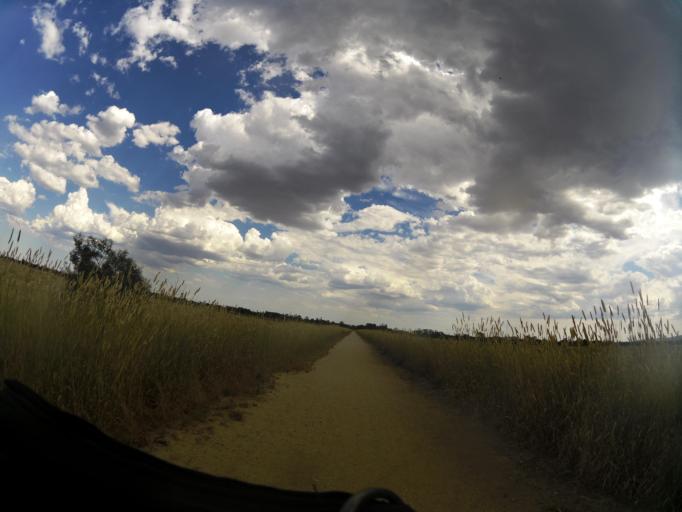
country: AU
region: Victoria
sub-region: Wellington
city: Heyfield
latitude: -38.0003
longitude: 146.6983
